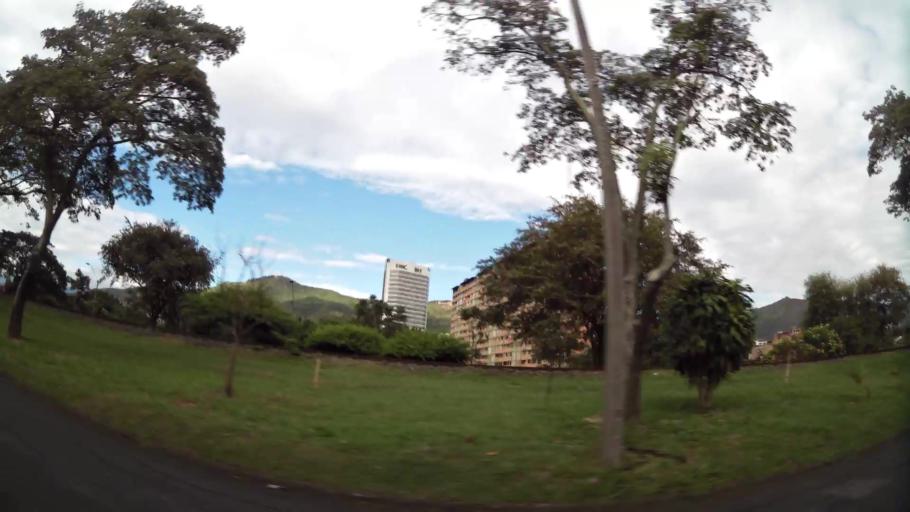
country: CO
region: Valle del Cauca
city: Cali
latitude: 3.4748
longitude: -76.5238
